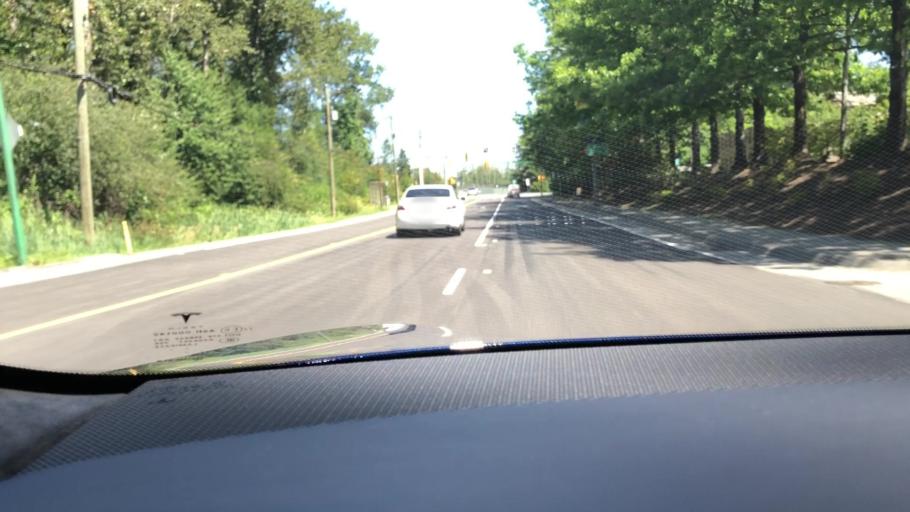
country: CA
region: British Columbia
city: Burnaby
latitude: 49.2499
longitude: -122.9689
